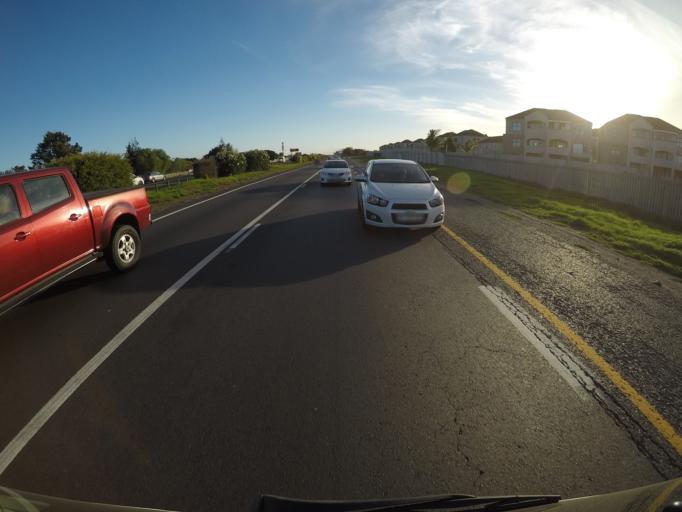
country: ZA
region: Western Cape
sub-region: City of Cape Town
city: Kraaifontein
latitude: -33.8622
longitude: 18.6887
